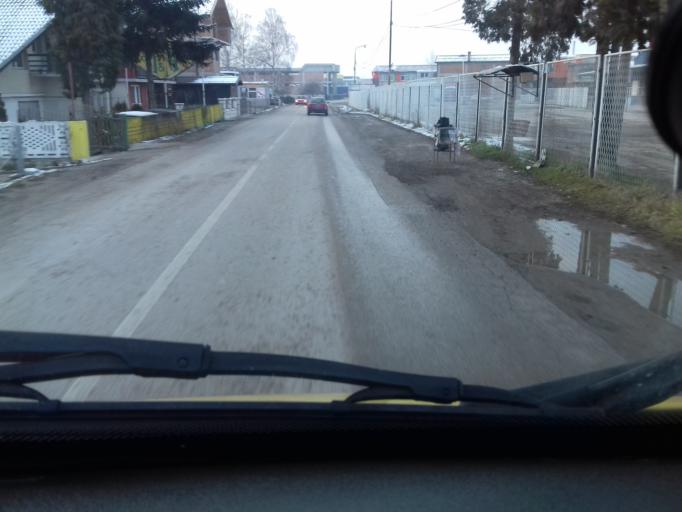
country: BA
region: Federation of Bosnia and Herzegovina
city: Visoko
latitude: 43.9992
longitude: 18.1787
